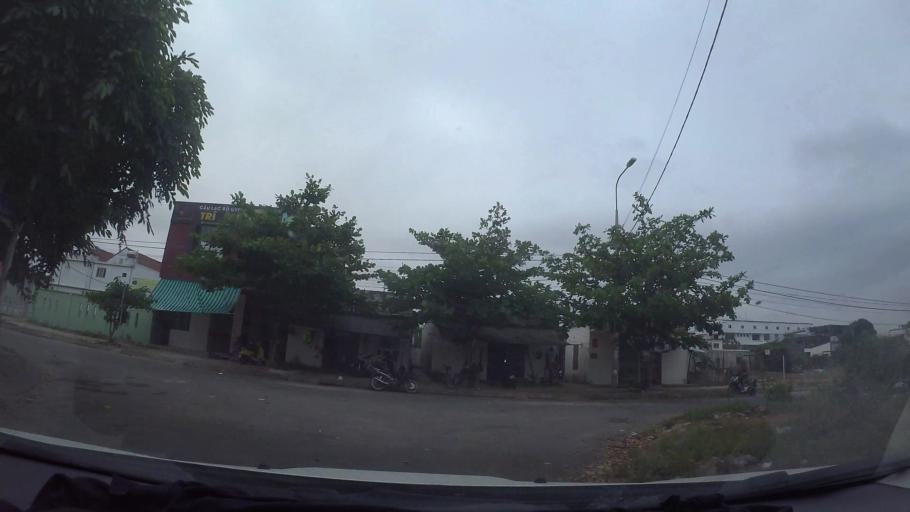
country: VN
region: Da Nang
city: Lien Chieu
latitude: 16.0878
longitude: 108.1529
